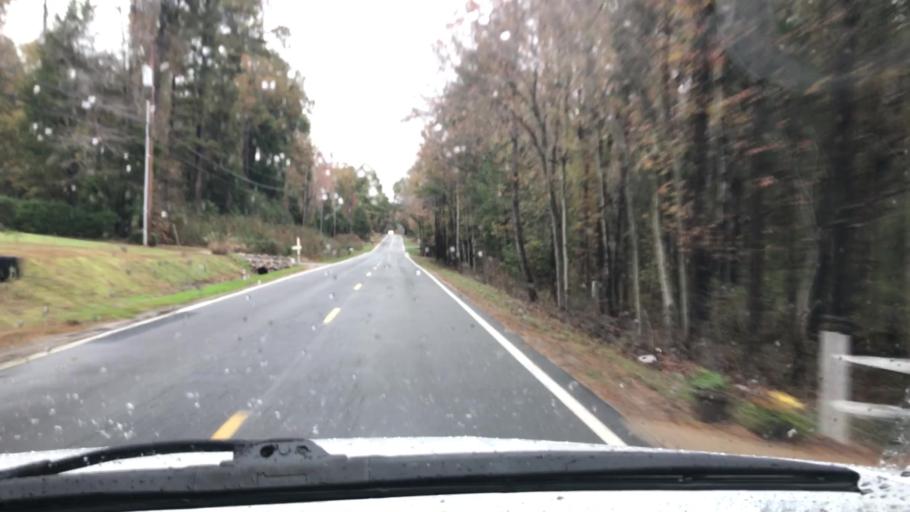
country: US
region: Virginia
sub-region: Henrico County
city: Short Pump
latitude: 37.6257
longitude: -77.6894
